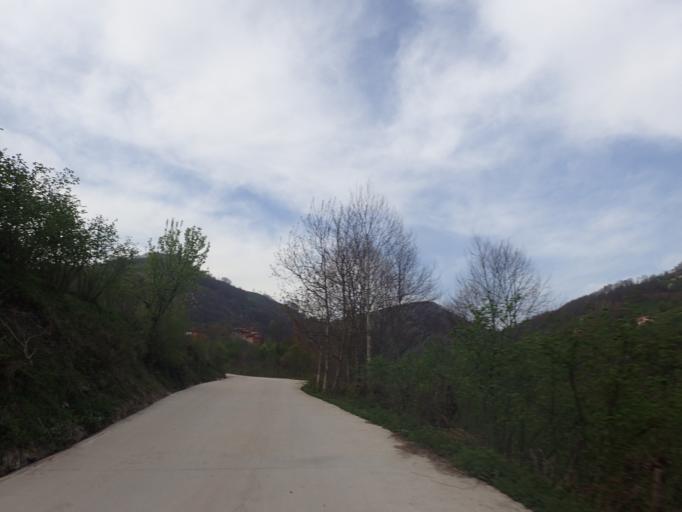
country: TR
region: Ordu
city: Aybasti
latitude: 40.7165
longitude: 37.2798
